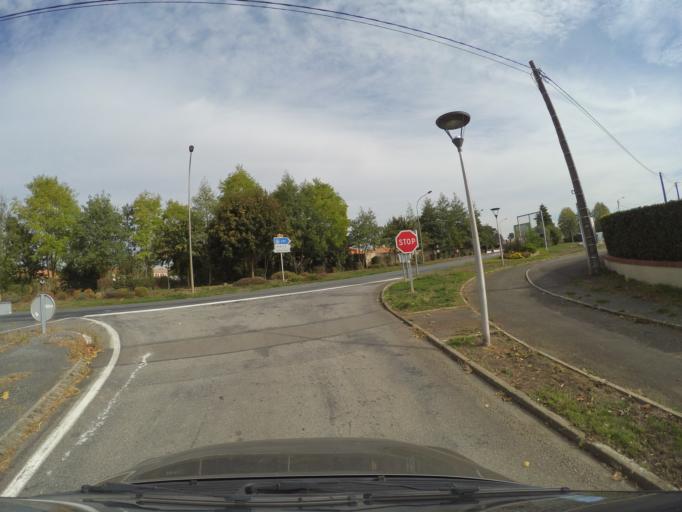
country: FR
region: Pays de la Loire
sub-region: Departement de Maine-et-Loire
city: Jallais
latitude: 47.1979
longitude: -0.8786
